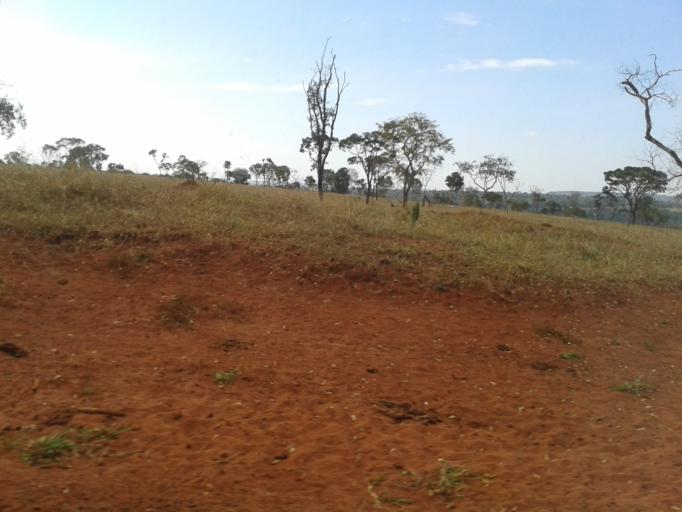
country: BR
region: Minas Gerais
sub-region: Ituiutaba
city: Ituiutaba
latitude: -19.0728
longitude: -49.3637
